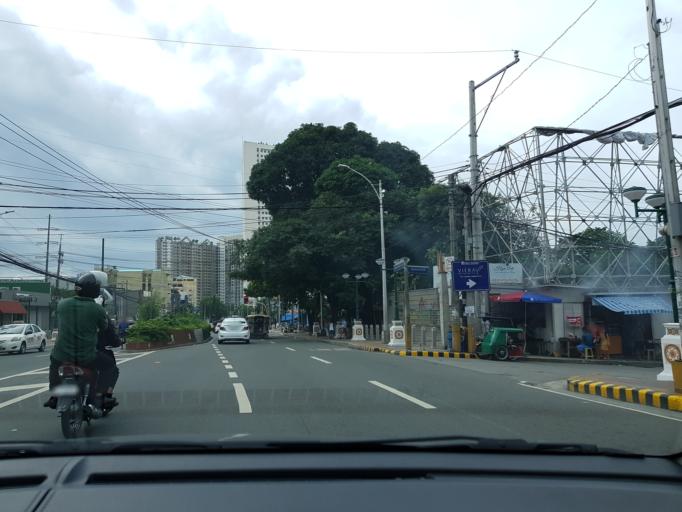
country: PH
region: Calabarzon
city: Del Monte
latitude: 14.6284
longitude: 121.0339
